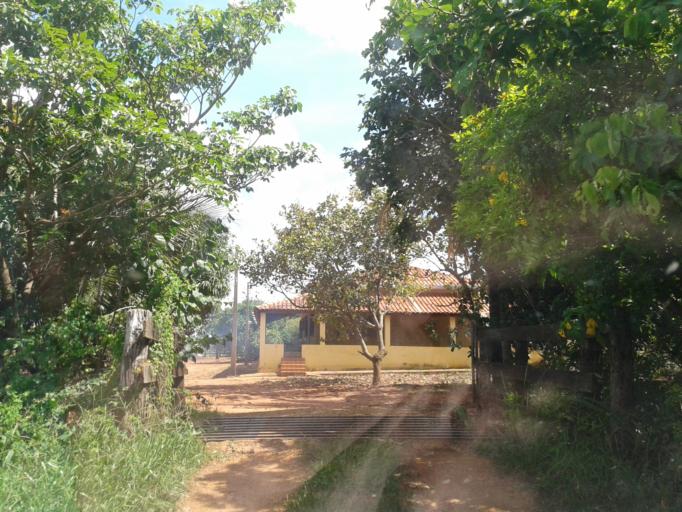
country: BR
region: Minas Gerais
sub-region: Santa Vitoria
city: Santa Vitoria
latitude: -19.1638
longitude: -50.5920
